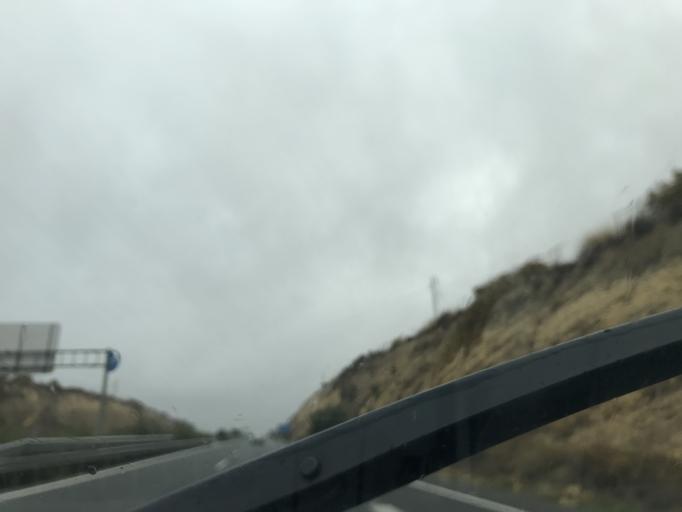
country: ES
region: Andalusia
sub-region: Provincia de Malaga
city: Mollina
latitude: 37.1204
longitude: -4.6716
